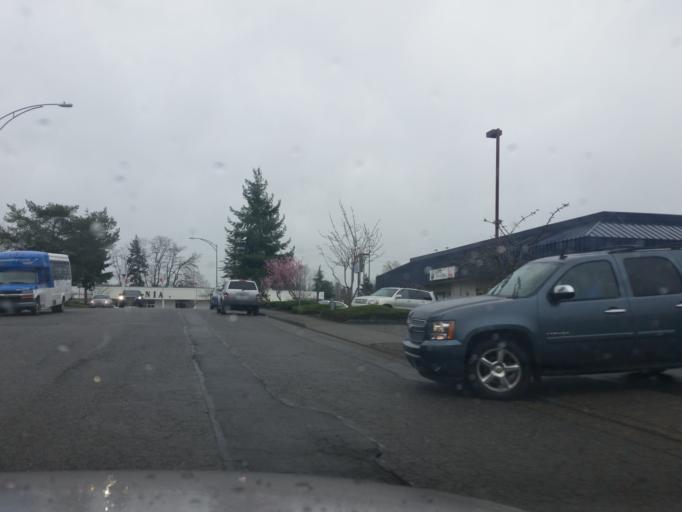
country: US
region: Washington
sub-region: Snohomish County
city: Alderwood Manor
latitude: 47.8194
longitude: -122.2888
